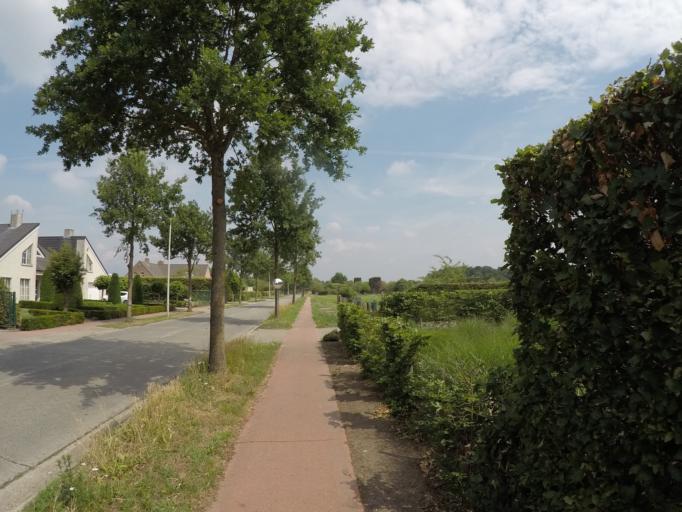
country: BE
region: Flanders
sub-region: Provincie Antwerpen
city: Brecht
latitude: 51.3723
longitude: 4.6443
